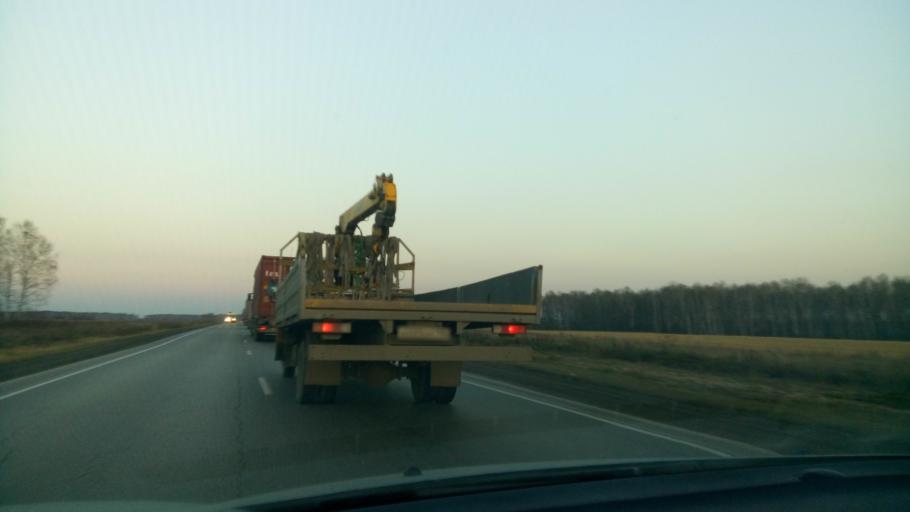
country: RU
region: Sverdlovsk
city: Pyshma
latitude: 56.9006
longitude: 63.0784
